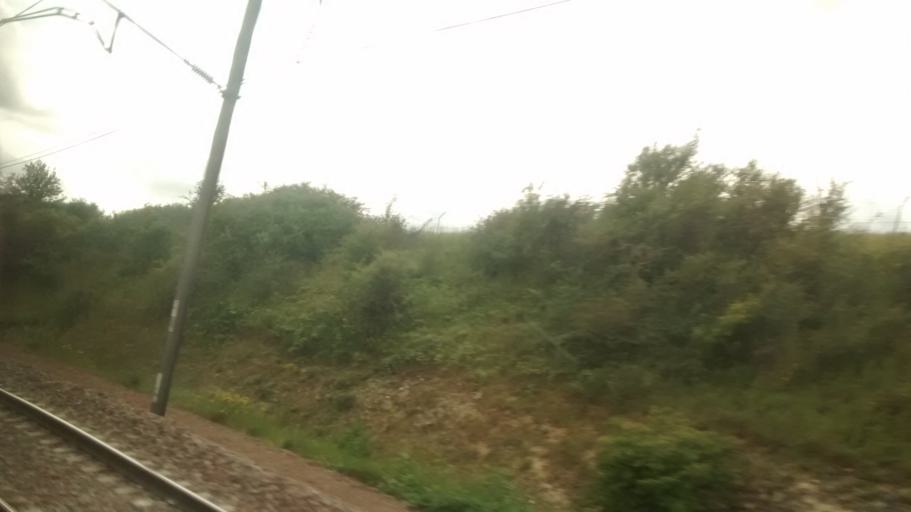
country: FR
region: Ile-de-France
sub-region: Departement des Yvelines
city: Ablis
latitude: 48.4849
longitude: 1.8767
